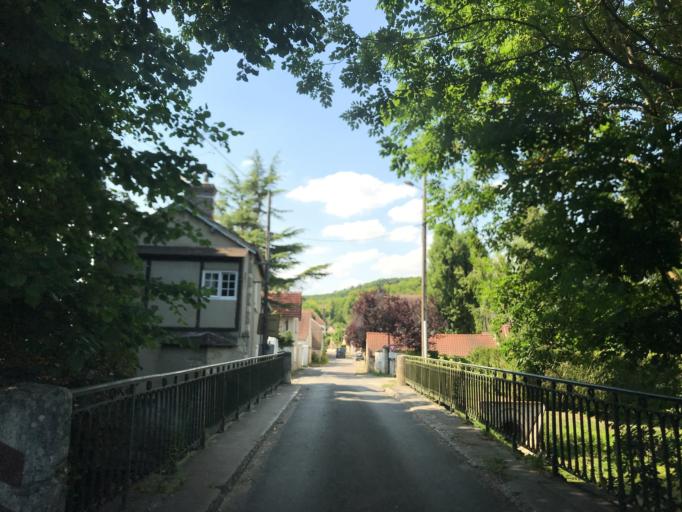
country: FR
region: Haute-Normandie
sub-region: Departement de l'Eure
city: Gasny
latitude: 49.0806
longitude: 1.5872
